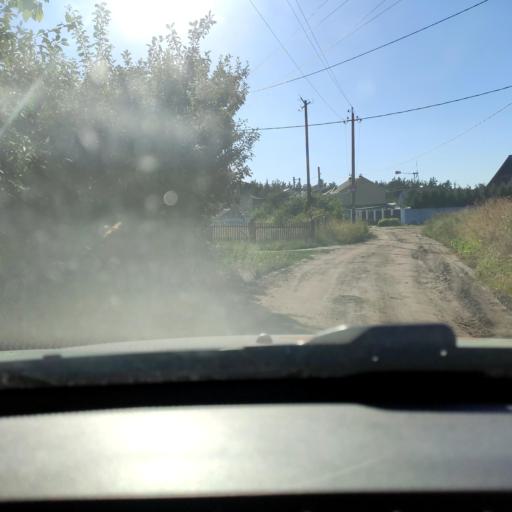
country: RU
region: Voronezj
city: Pridonskoy
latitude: 51.6312
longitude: 39.0885
